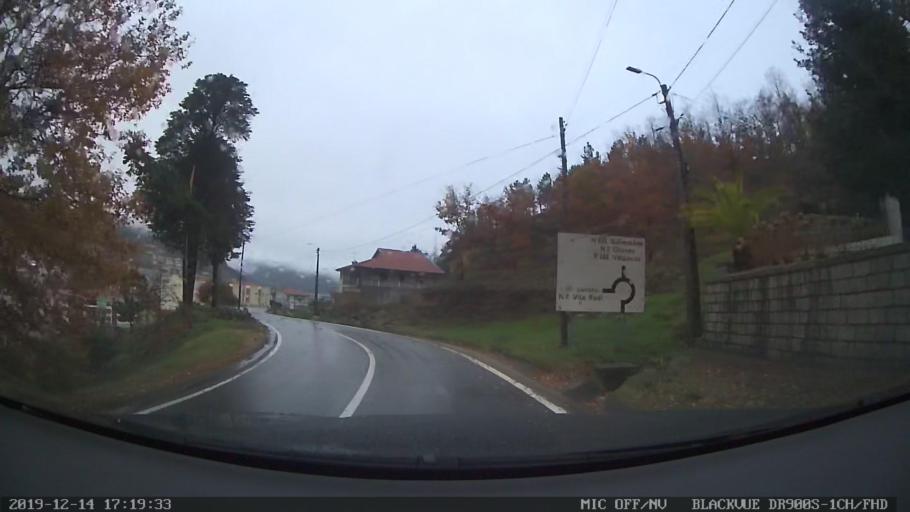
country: PT
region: Vila Real
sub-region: Vila Pouca de Aguiar
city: Vila Pouca de Aguiar
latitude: 41.4960
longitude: -7.6406
